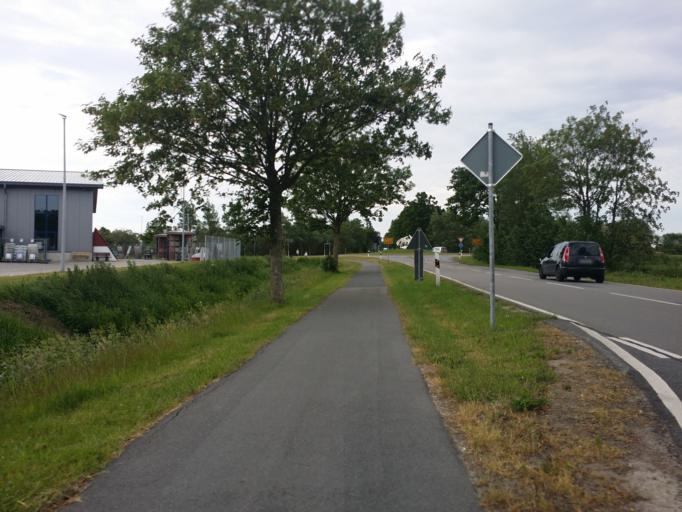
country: DE
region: Lower Saxony
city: Wittmund
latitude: 53.5842
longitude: 7.7827
